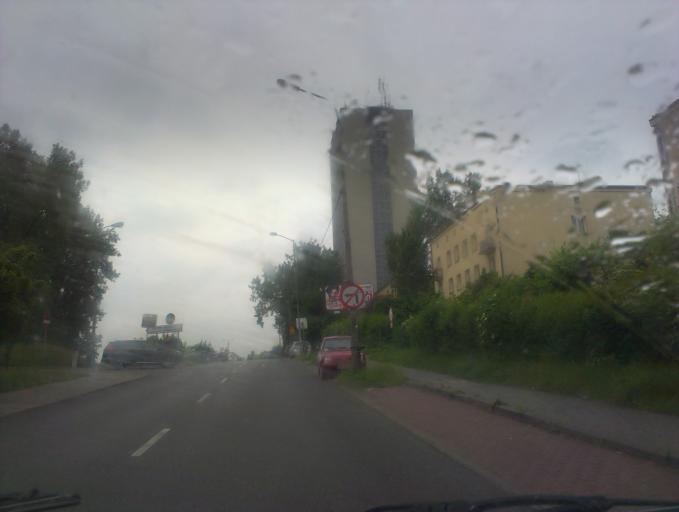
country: PL
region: Silesian Voivodeship
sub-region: Katowice
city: Katowice
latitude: 50.2488
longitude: 19.0173
